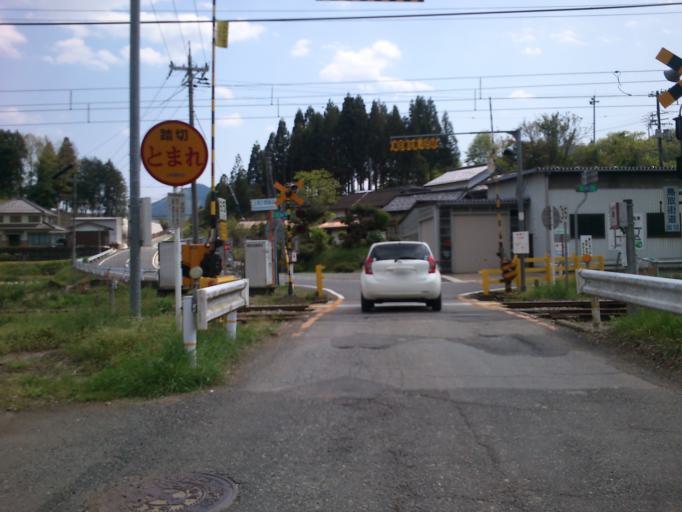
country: JP
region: Kyoto
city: Fukuchiyama
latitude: 35.3420
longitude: 134.9335
